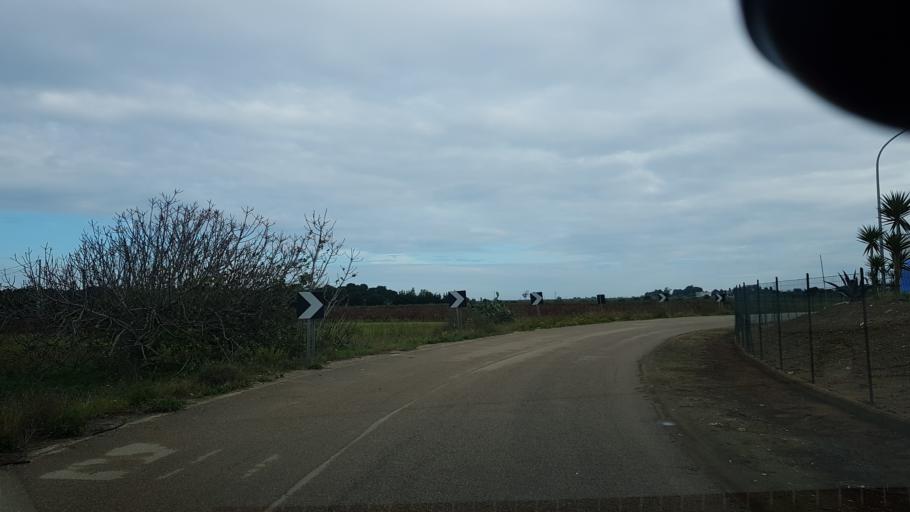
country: IT
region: Apulia
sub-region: Provincia di Brindisi
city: Brindisi
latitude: 40.6621
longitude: 17.8882
